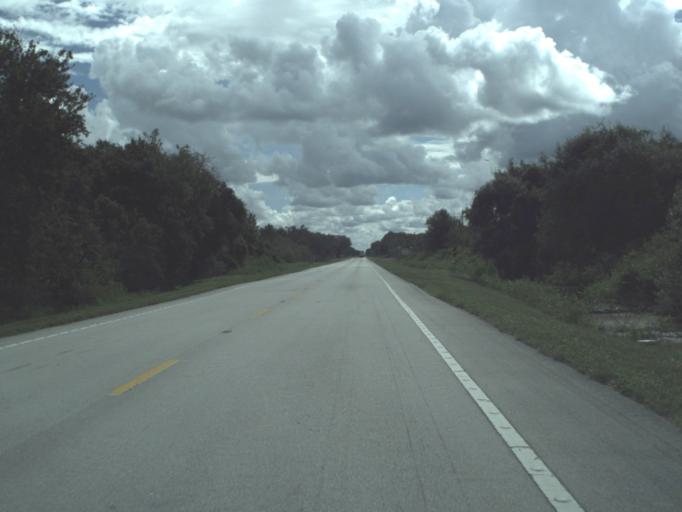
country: US
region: Florida
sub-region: DeSoto County
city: Arcadia
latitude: 27.2880
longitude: -82.0466
